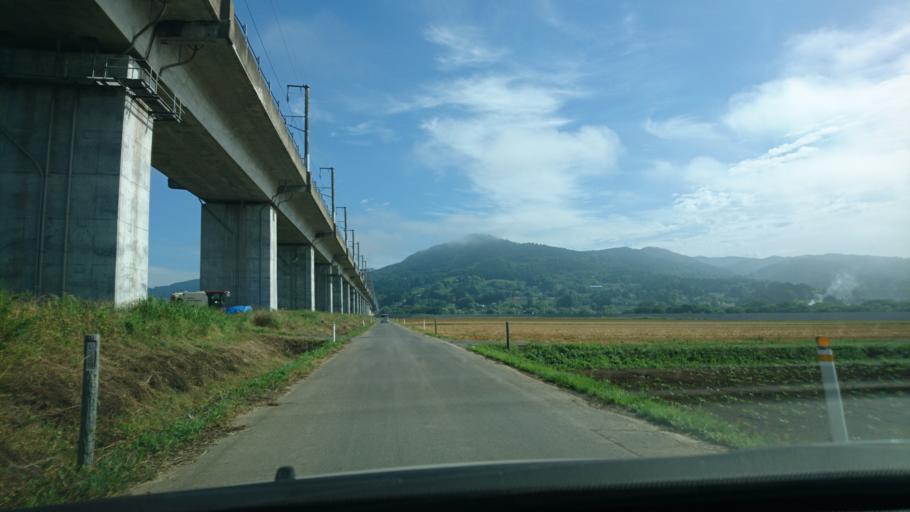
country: JP
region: Iwate
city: Ichinoseki
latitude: 38.9665
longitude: 141.1536
